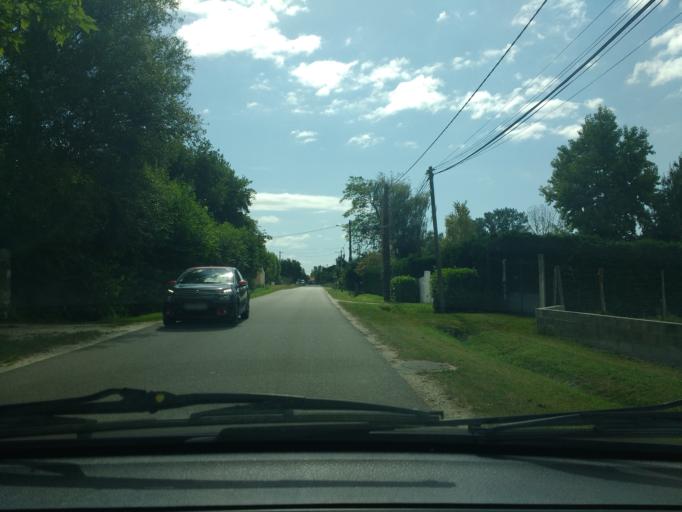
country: FR
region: Aquitaine
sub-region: Departement de la Gironde
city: Salles
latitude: 44.5611
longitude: -0.8495
